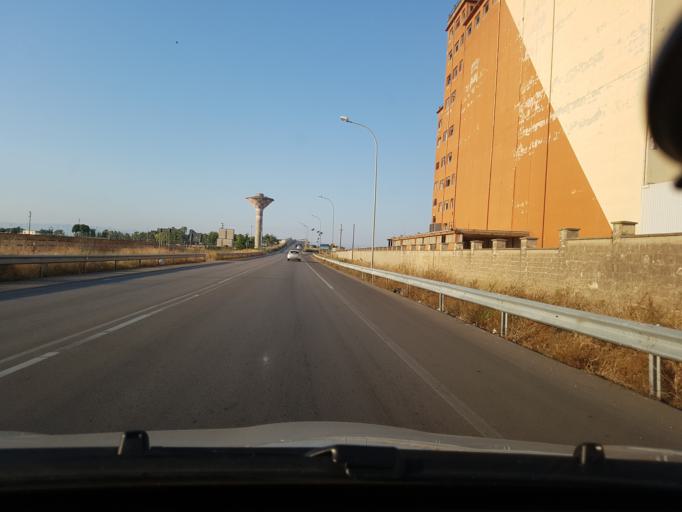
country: IT
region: Apulia
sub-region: Provincia di Foggia
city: Carapelle
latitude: 41.4028
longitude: 15.6504
